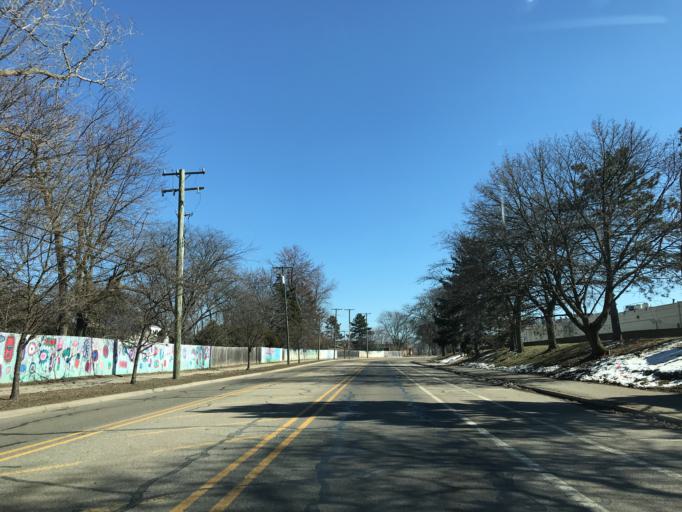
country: US
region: Michigan
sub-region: Washtenaw County
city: Ann Arbor
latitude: 42.3047
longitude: -83.7061
